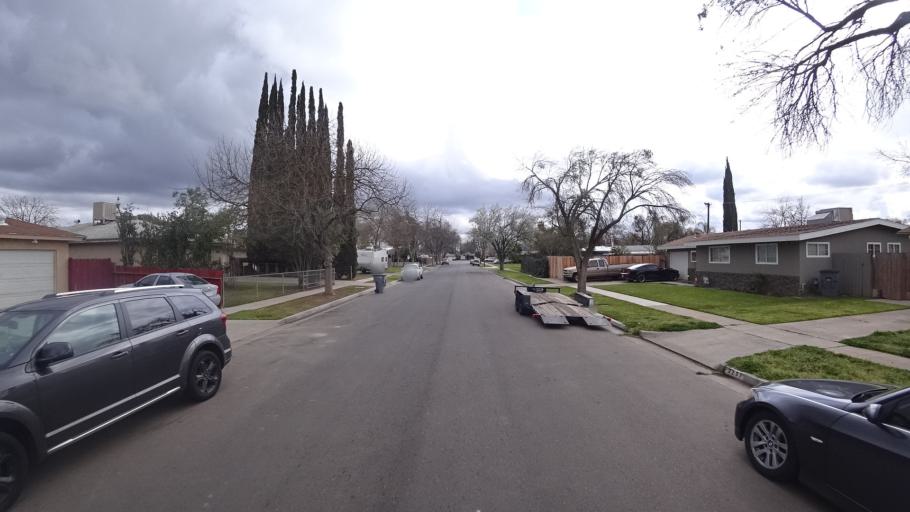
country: US
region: California
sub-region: Fresno County
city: West Park
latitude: 36.7829
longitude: -119.8376
